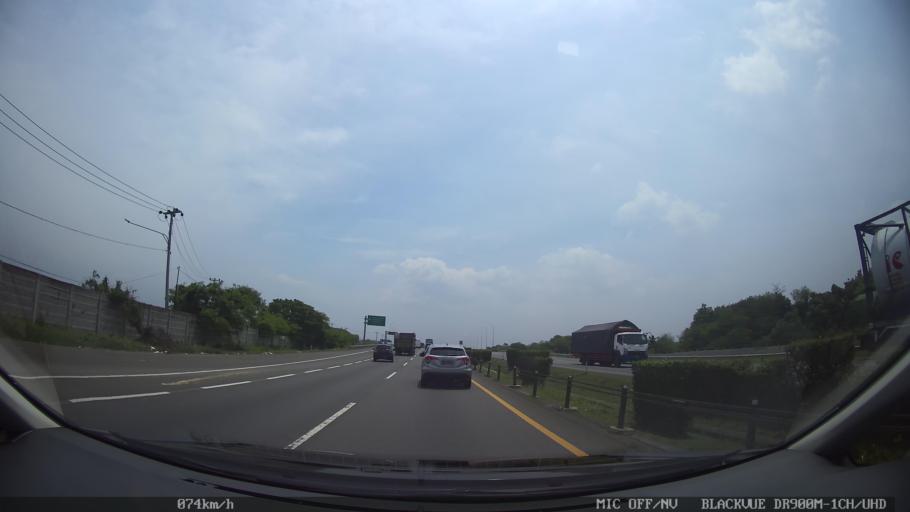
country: ID
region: Banten
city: Serang
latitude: -6.1388
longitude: 106.2543
